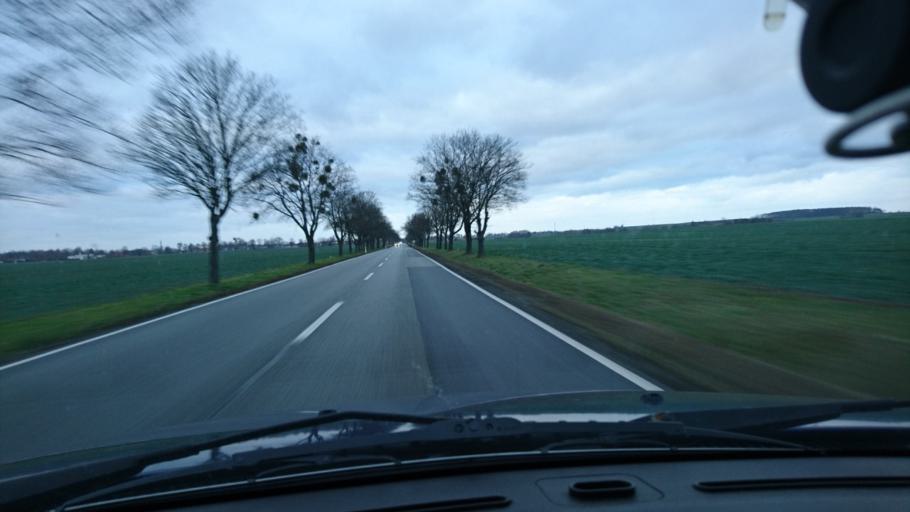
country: PL
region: Opole Voivodeship
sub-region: Powiat kluczborski
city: Byczyna
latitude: 51.0725
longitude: 18.2027
